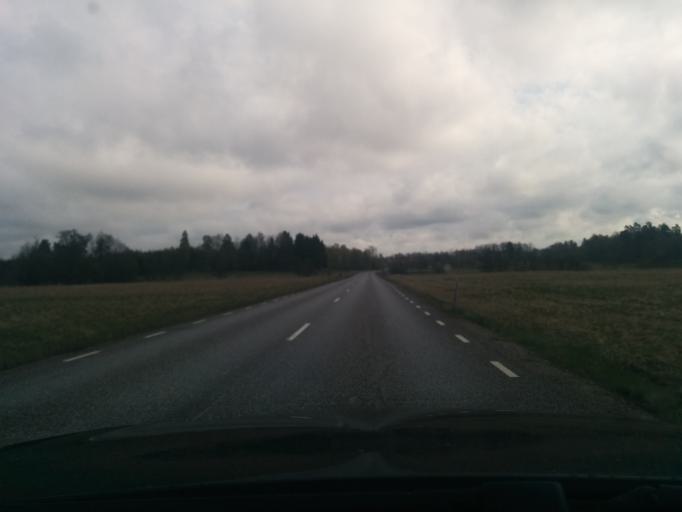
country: SE
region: Uppsala
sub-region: Tierps Kommun
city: Orbyhus
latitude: 60.1949
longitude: 17.6892
